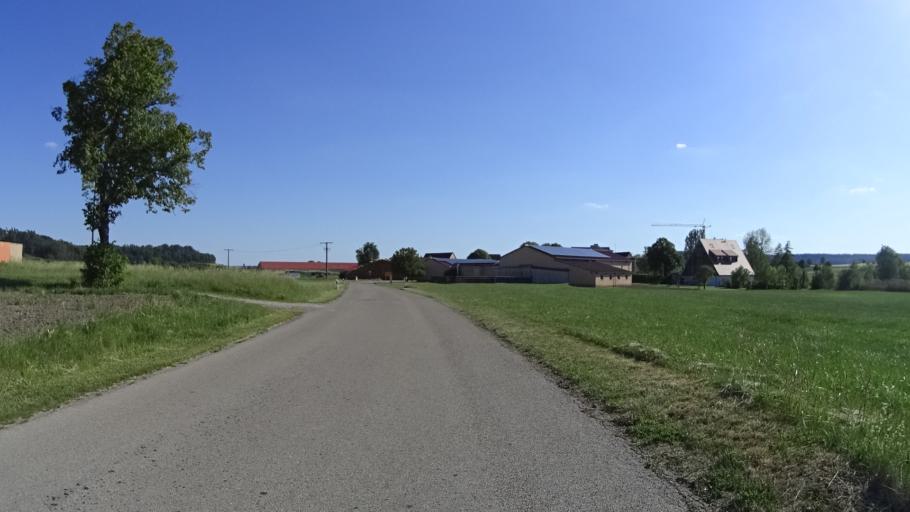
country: DE
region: Bavaria
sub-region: Regierungsbezirk Mittelfranken
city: Feuchtwangen
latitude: 49.1937
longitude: 10.3225
